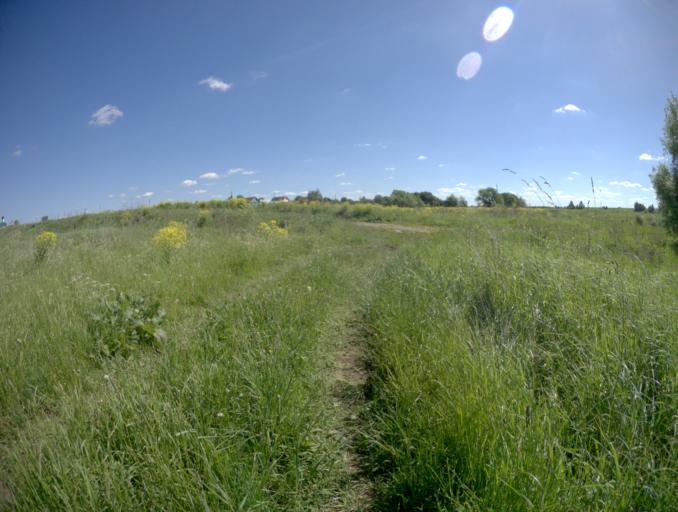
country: RU
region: Ivanovo
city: Gavrilov Posad
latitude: 56.5166
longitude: 40.2118
